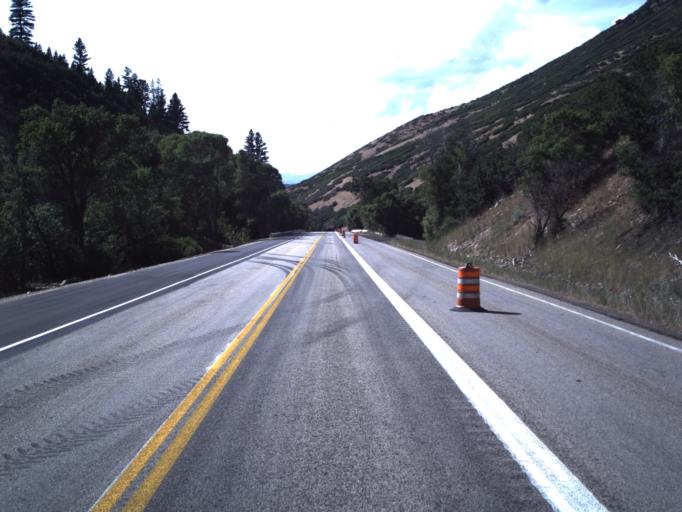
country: US
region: Utah
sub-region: Wasatch County
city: Heber
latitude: 40.4083
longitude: -111.3147
